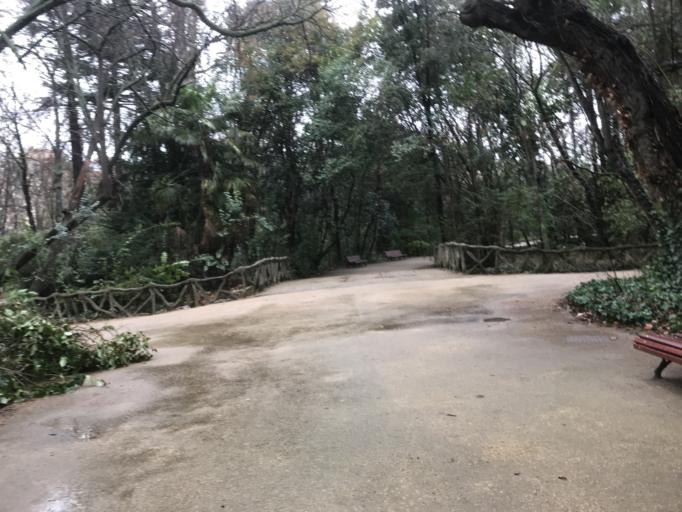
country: ES
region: Castille and Leon
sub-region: Provincia de Valladolid
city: Valladolid
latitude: 41.6448
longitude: -4.7320
